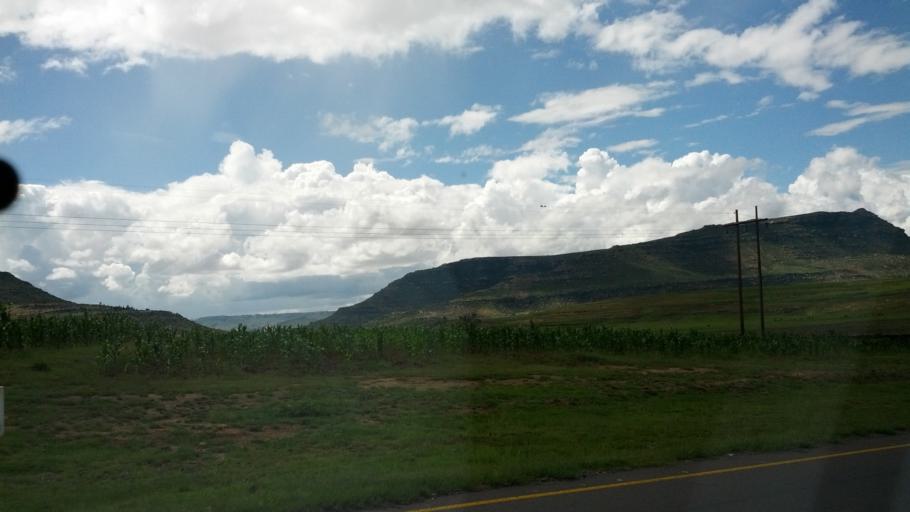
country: LS
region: Maseru
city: Maseru
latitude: -29.5513
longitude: 27.4973
